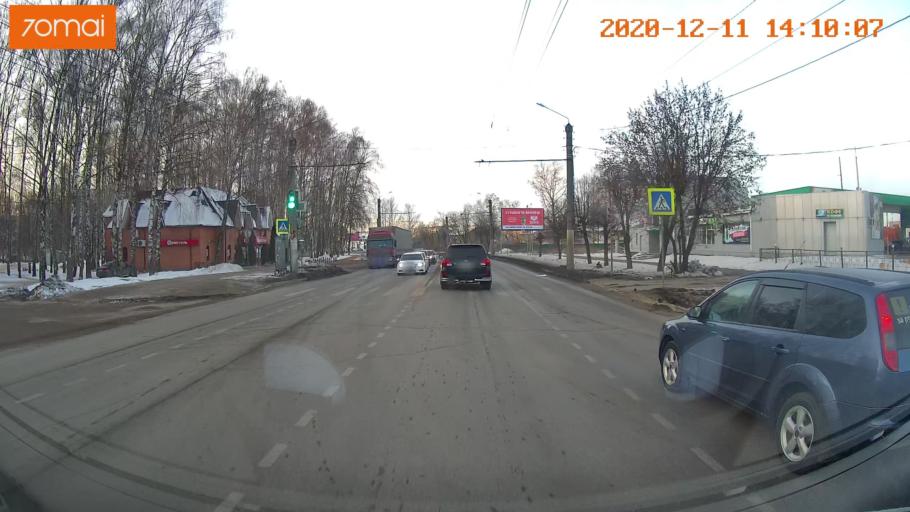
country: RU
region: Kostroma
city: Oktyabr'skiy
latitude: 57.7400
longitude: 40.9857
